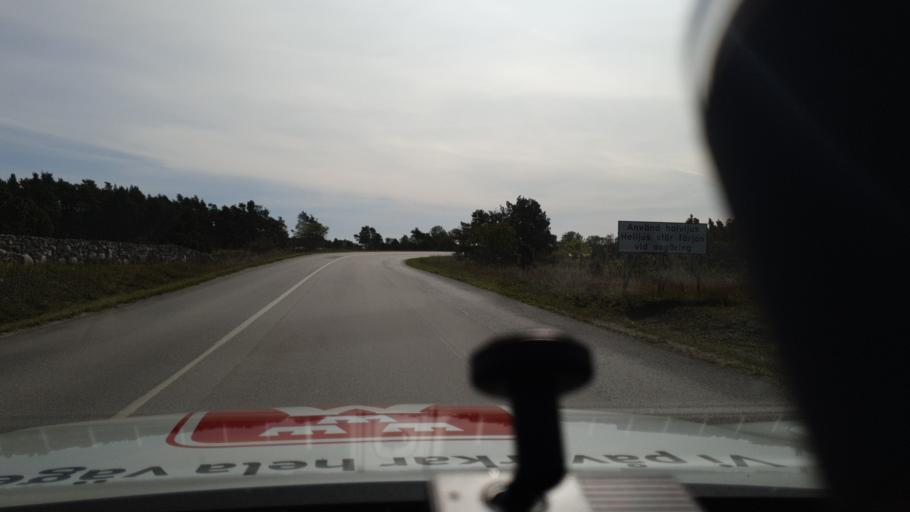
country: SE
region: Gotland
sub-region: Gotland
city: Slite
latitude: 57.8727
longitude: 19.0857
